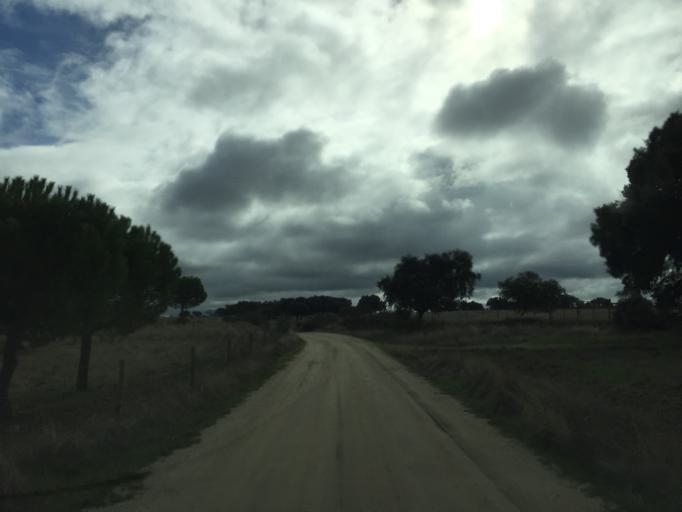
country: PT
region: Portalegre
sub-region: Alter do Chao
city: Alter do Chao
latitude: 39.2396
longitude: -7.6998
